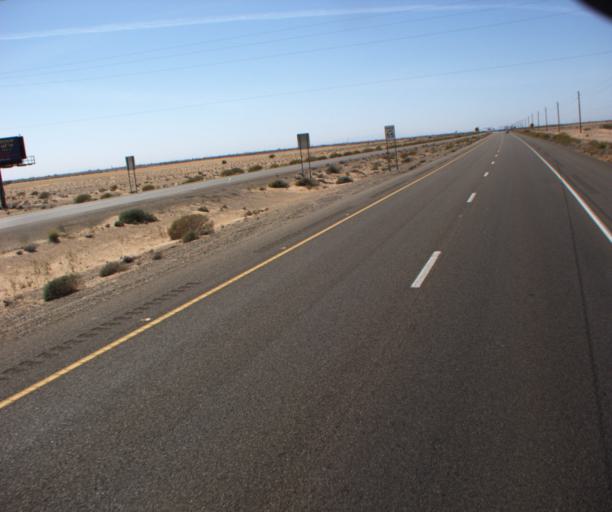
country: MX
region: Sonora
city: San Luis Rio Colorado
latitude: 32.4948
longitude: -114.6916
